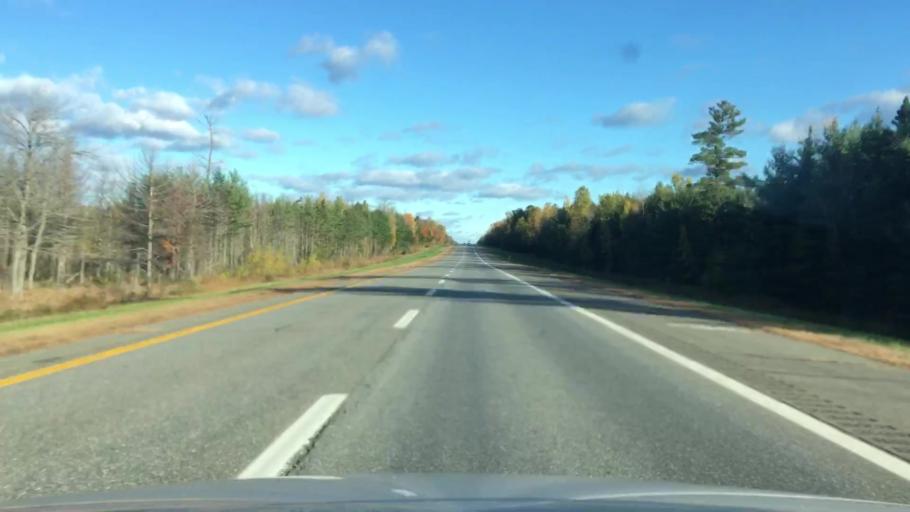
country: US
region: Maine
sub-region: Penobscot County
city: Greenbush
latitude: 45.0634
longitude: -68.6889
